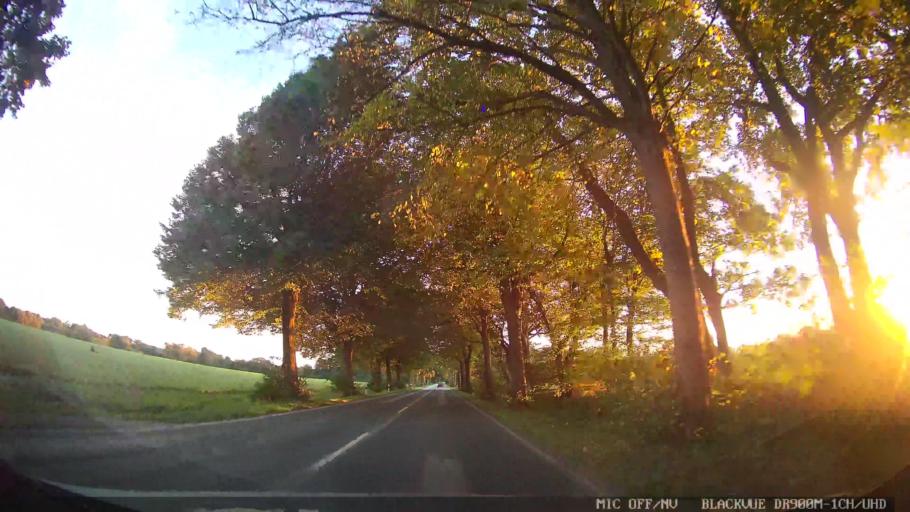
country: DE
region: Schleswig-Holstein
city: Susel
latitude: 54.0648
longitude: 10.6871
